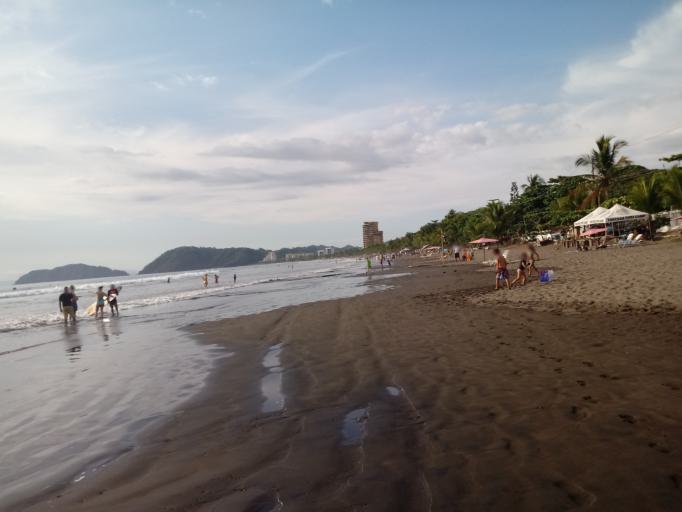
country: CR
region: Puntarenas
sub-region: Canton de Garabito
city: Jaco
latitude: 9.6020
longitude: -84.6213
